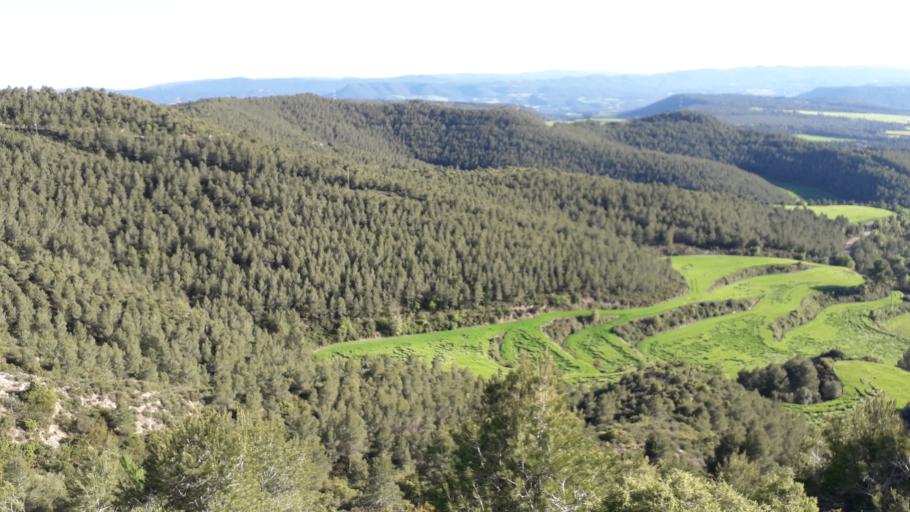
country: ES
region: Catalonia
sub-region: Provincia de Barcelona
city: Jorba
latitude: 41.6371
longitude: 1.5785
